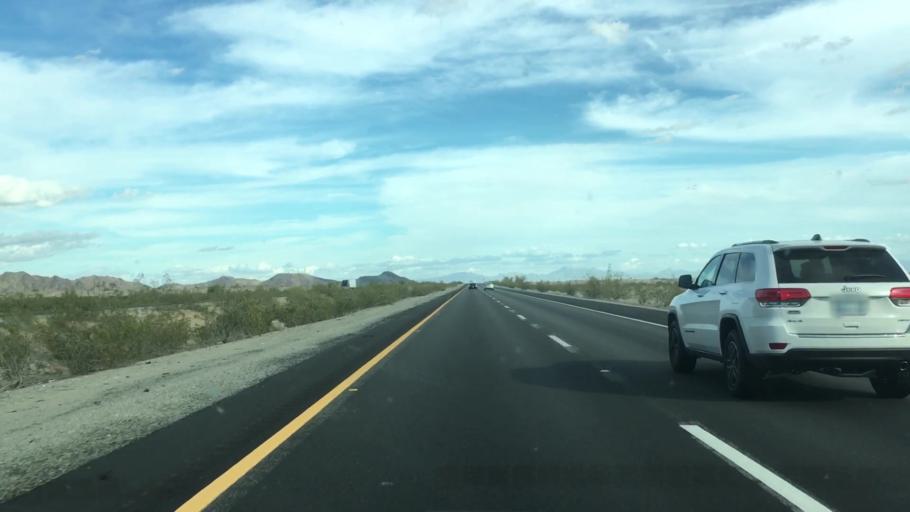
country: US
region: California
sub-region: Riverside County
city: Mesa Verde
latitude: 33.6095
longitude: -114.8232
